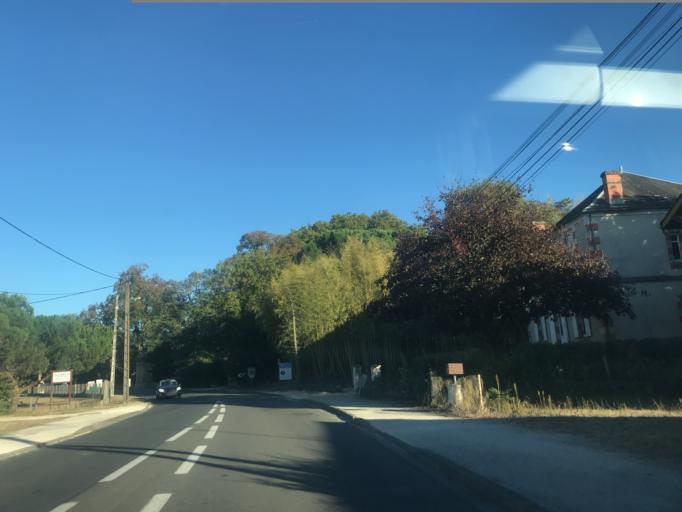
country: FR
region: Poitou-Charentes
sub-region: Departement de la Charente-Maritime
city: Saint-Aigulin
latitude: 45.1566
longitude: -0.0016
